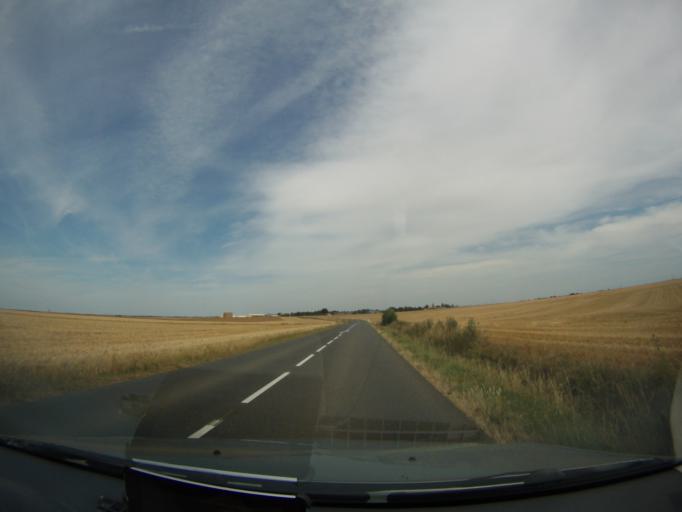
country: FR
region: Poitou-Charentes
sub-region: Departement de la Vienne
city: Moncontour
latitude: 46.8109
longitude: -0.0493
